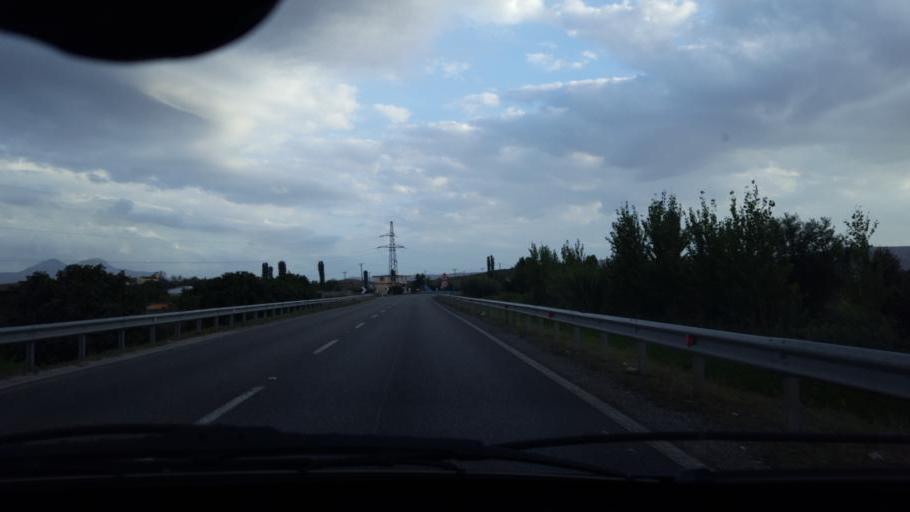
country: AL
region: Shkoder
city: Vukatane
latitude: 41.9760
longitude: 19.5464
